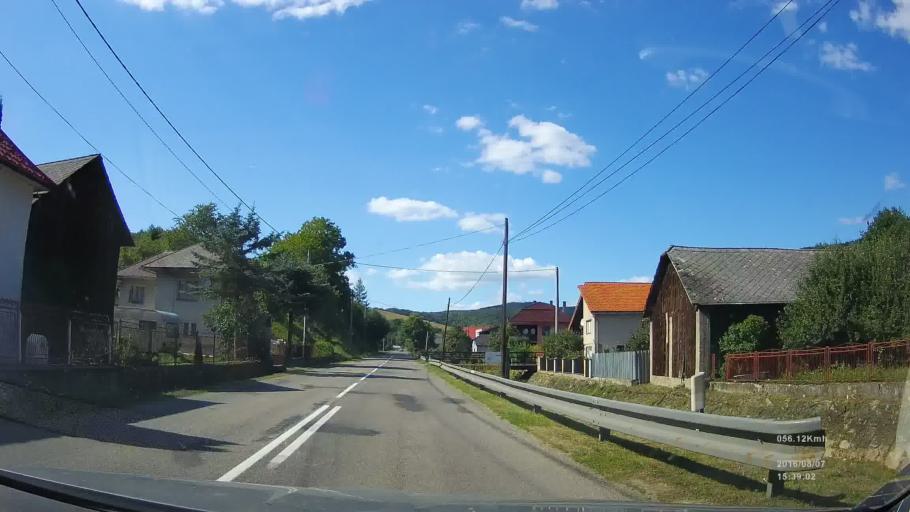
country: SK
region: Presovsky
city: Giraltovce
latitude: 49.1152
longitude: 21.6064
